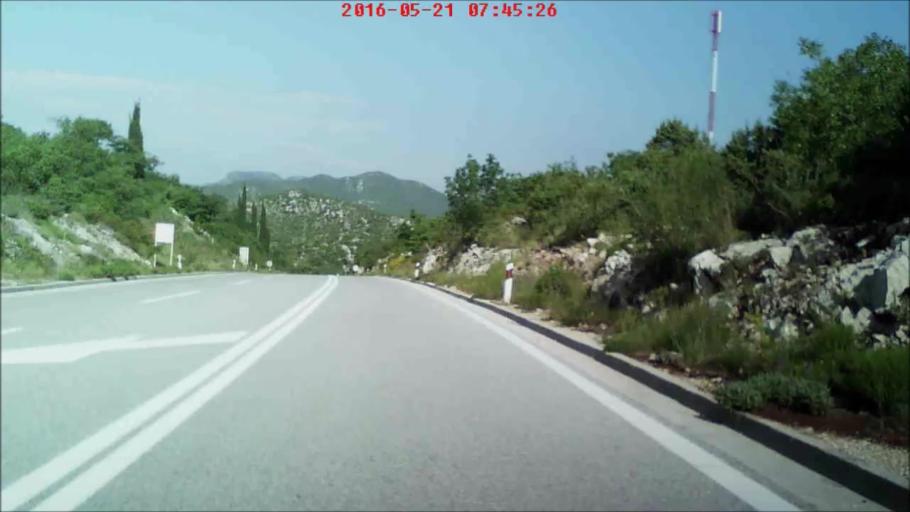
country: HR
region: Dubrovacko-Neretvanska
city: Ston
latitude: 42.8230
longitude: 17.7652
